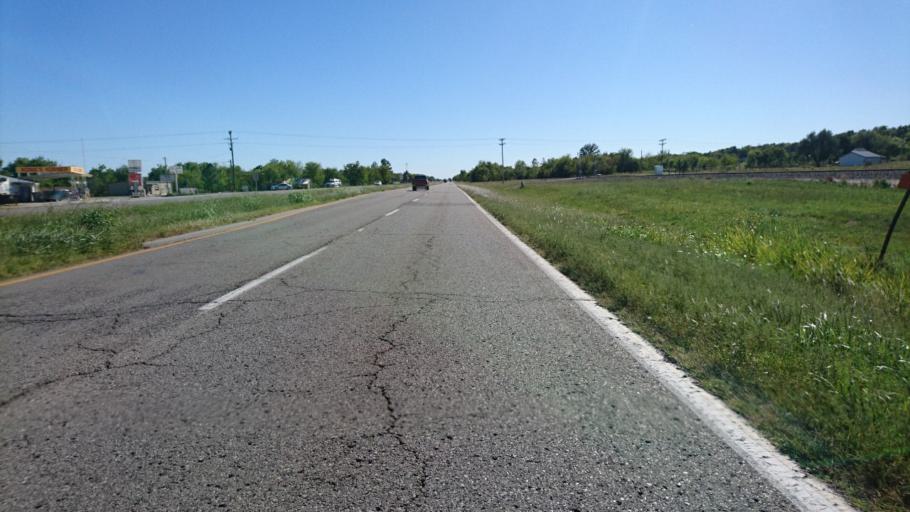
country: US
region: Oklahoma
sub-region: Rogers County
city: Bushyhead
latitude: 36.3958
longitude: -95.5485
